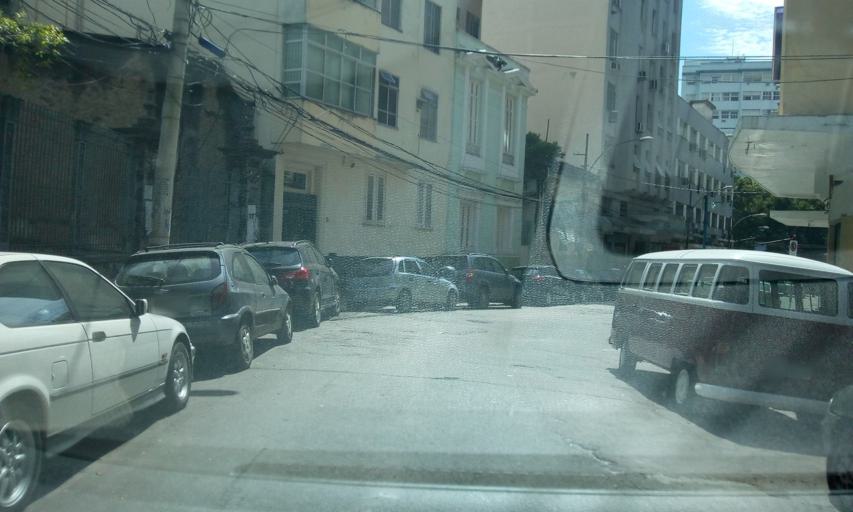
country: BR
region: Rio de Janeiro
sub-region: Rio De Janeiro
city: Rio de Janeiro
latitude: -22.9218
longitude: -43.1782
